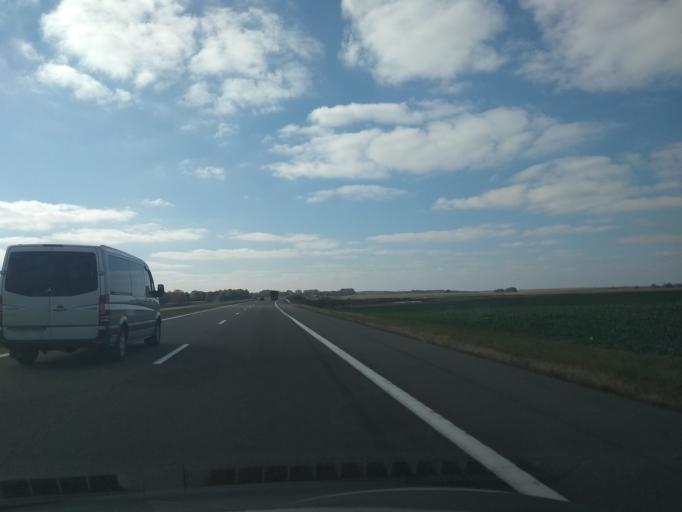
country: BY
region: Brest
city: Baranovichi
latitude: 53.2209
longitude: 26.1516
